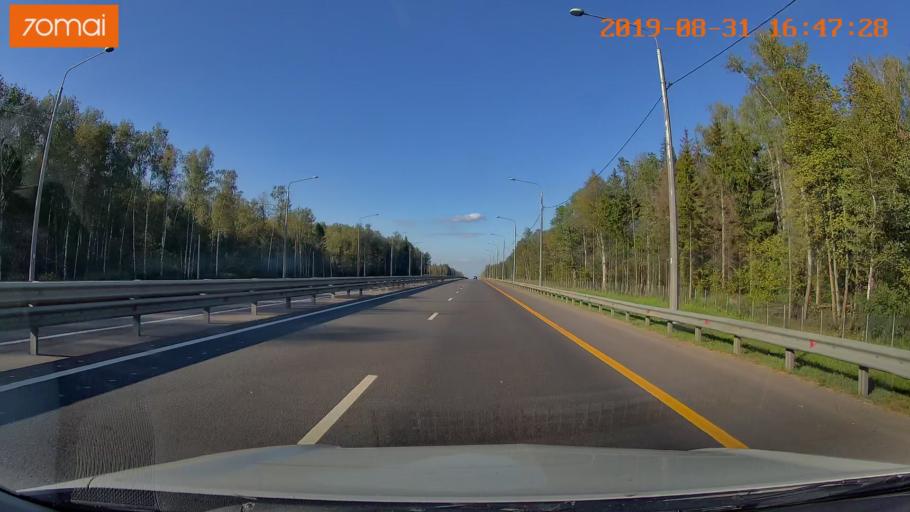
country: RU
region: Kaluga
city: Pyatovskiy
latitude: 54.6546
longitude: 36.1391
